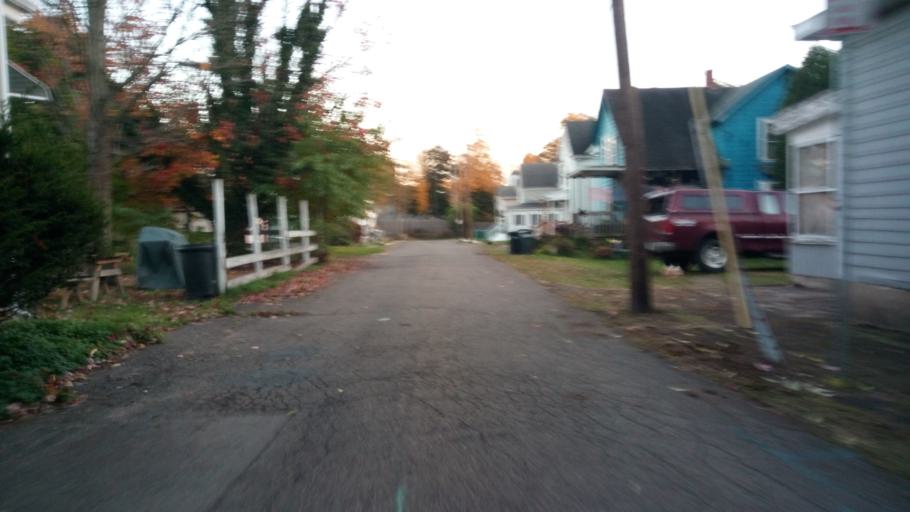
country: US
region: New York
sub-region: Chemung County
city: Elmira
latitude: 42.0790
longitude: -76.8049
